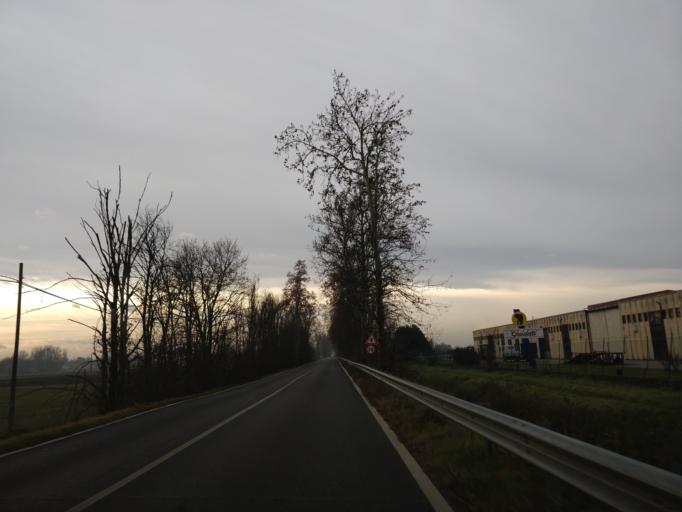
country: IT
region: Emilia-Romagna
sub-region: Provincia di Ferrara
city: Corpo Reno
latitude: 44.7664
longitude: 11.3076
